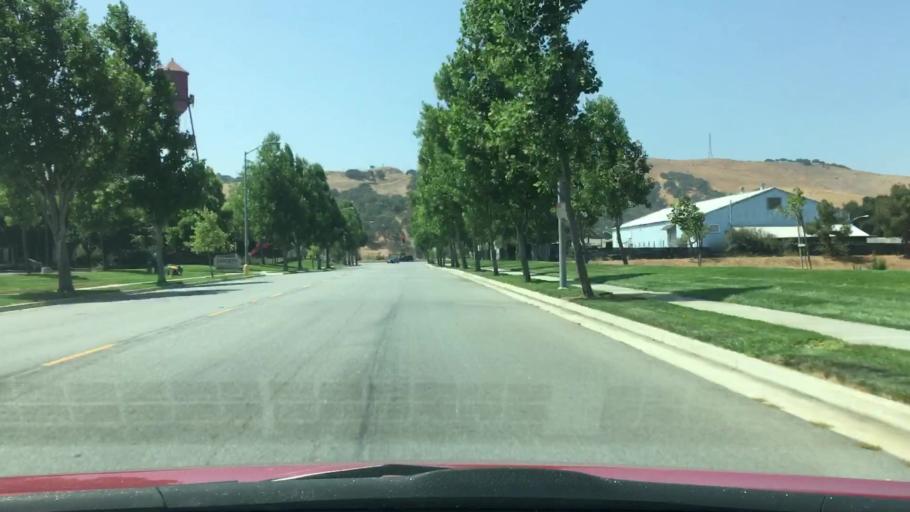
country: US
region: California
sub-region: Santa Clara County
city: Morgan Hill
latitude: 37.1498
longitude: -121.6672
